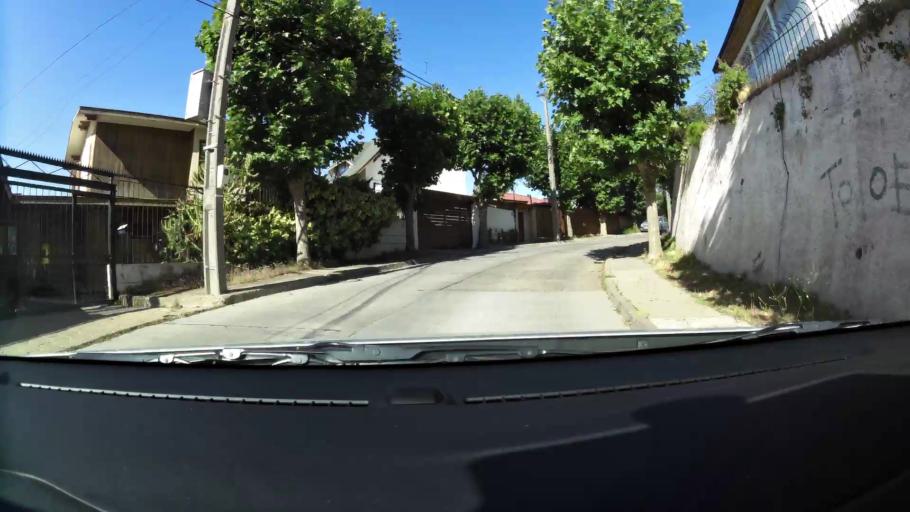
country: CL
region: Valparaiso
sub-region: Provincia de Valparaiso
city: Vina del Mar
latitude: -33.0345
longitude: -71.5559
